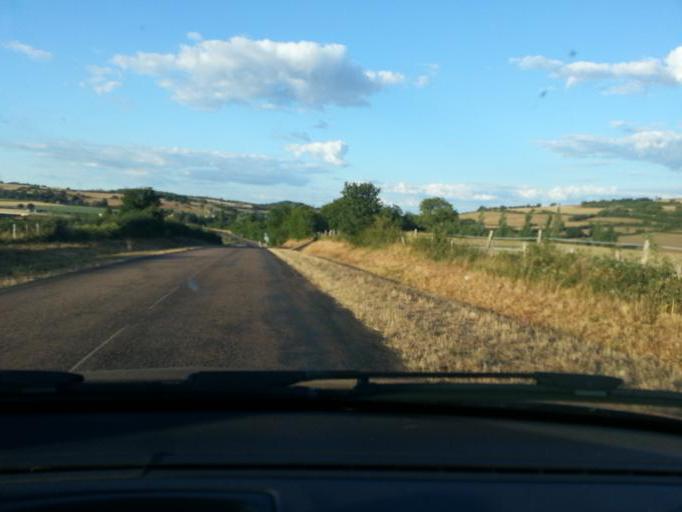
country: FR
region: Bourgogne
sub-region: Departement de Saone-et-Loire
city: Buxy
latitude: 46.7410
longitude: 4.6410
